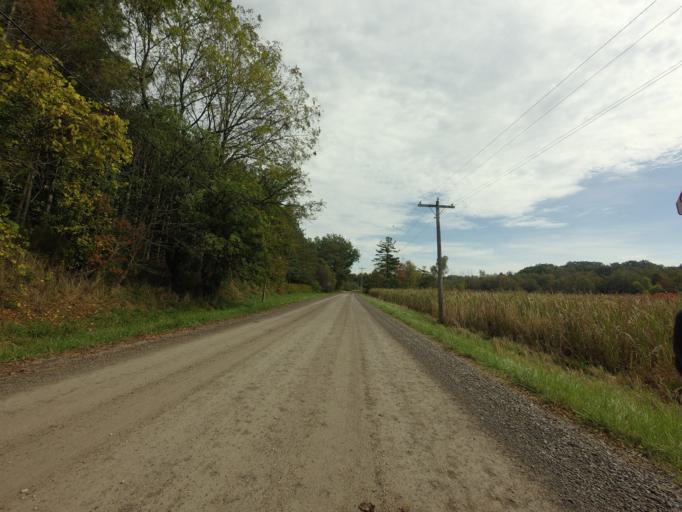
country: CA
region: Ontario
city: Ancaster
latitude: 43.2350
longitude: -80.0418
